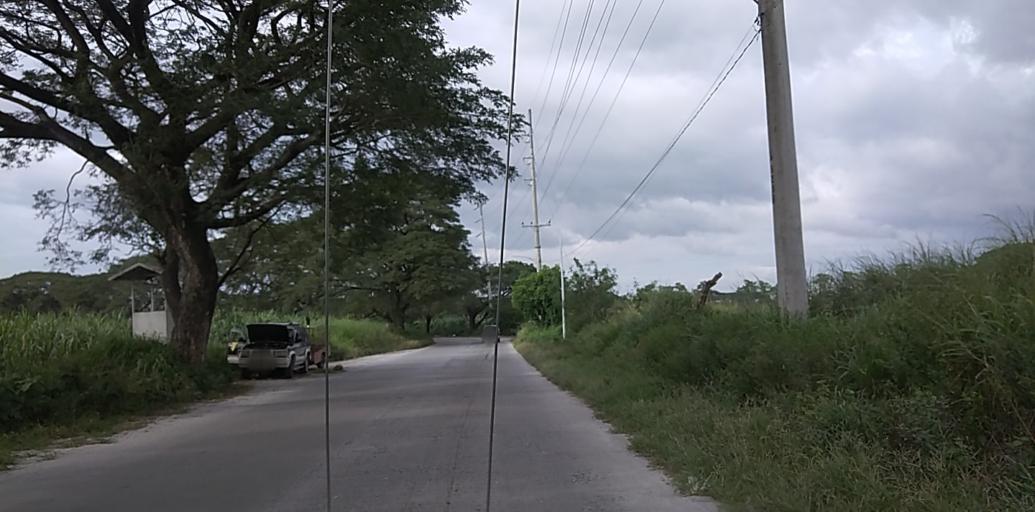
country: PH
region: Central Luzon
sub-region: Province of Pampanga
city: Porac
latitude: 15.0767
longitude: 120.5495
